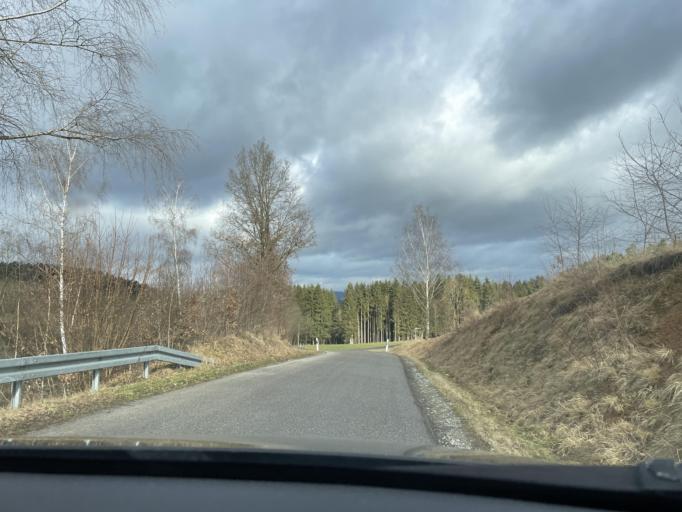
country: DE
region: Bavaria
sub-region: Lower Bavaria
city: Prackenbach
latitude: 49.1160
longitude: 12.8426
